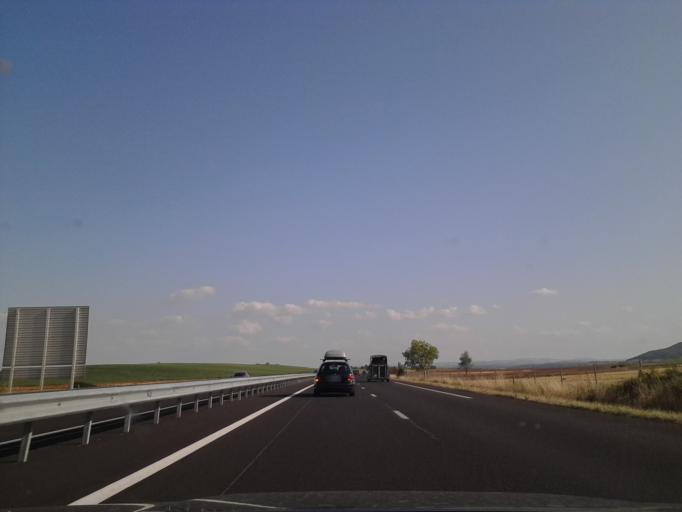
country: FR
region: Auvergne
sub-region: Departement du Puy-de-Dome
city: Le Breuil-sur-Couze
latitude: 45.4416
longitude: 3.2712
